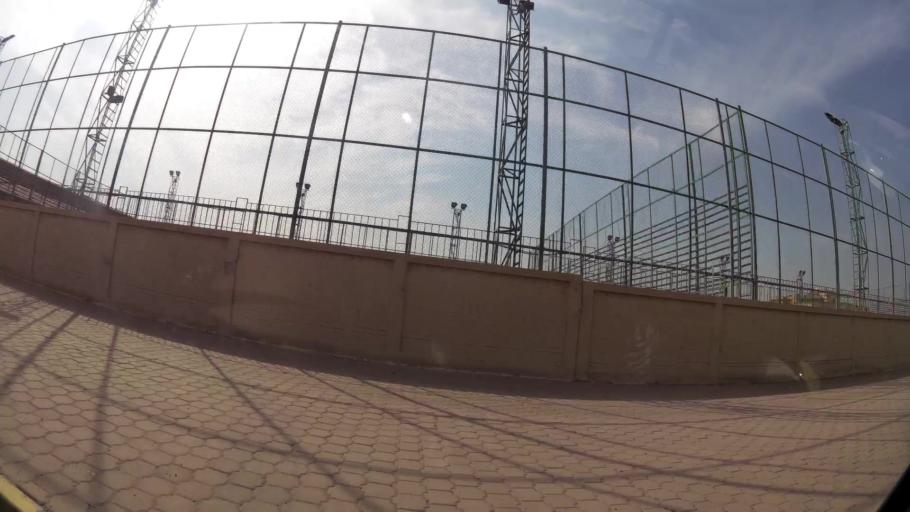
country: KW
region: Al Asimah
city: Ash Shamiyah
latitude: 29.3212
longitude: 47.9646
